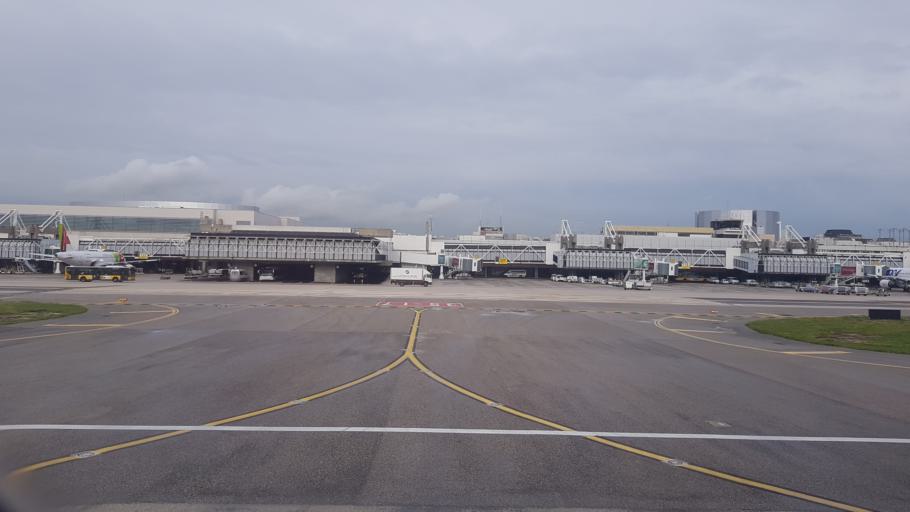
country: PT
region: Lisbon
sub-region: Loures
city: Moscavide
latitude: 38.7702
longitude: -9.1329
